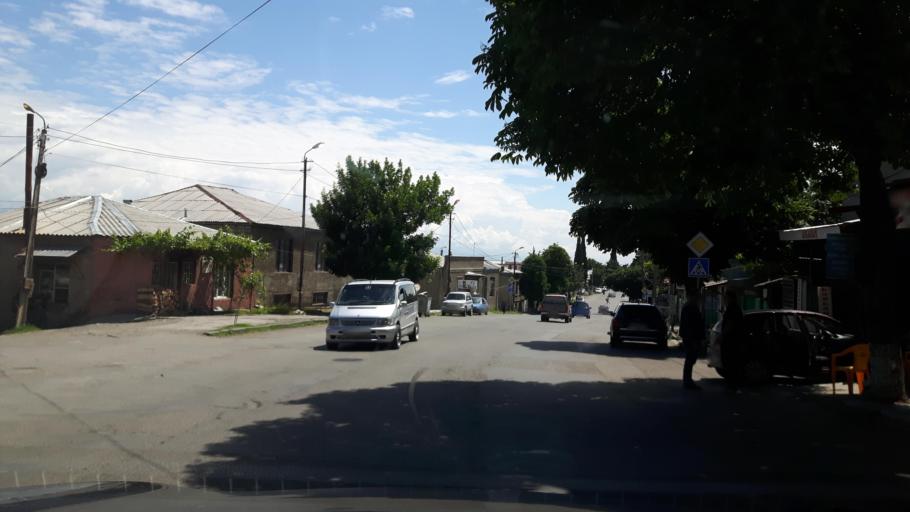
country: GE
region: Kakheti
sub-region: Telavi
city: Telavi
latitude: 41.9212
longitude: 45.4744
